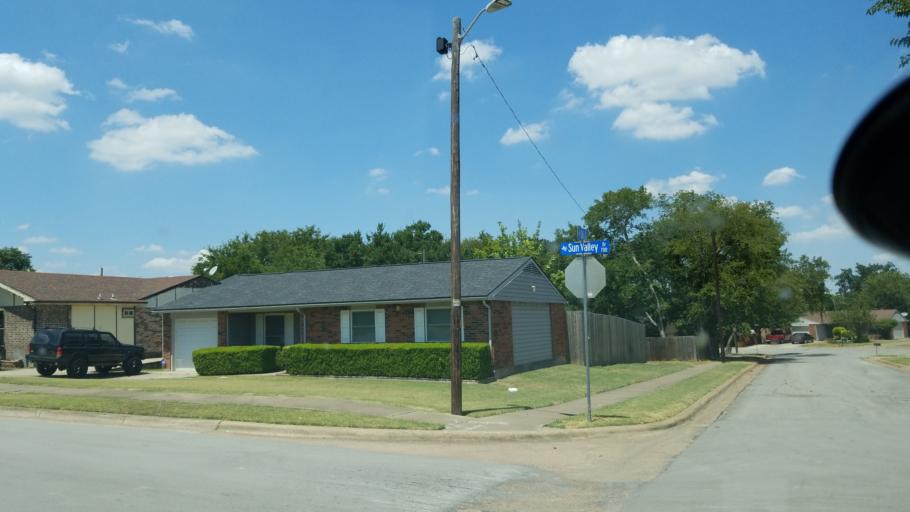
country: US
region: Texas
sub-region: Dallas County
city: Duncanville
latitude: 32.6681
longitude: -96.8921
